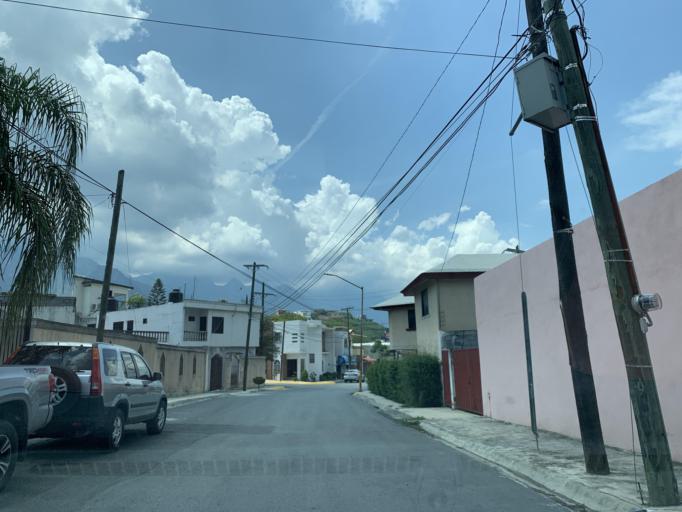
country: MX
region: Nuevo Leon
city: Santiago
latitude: 25.3990
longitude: -100.1288
